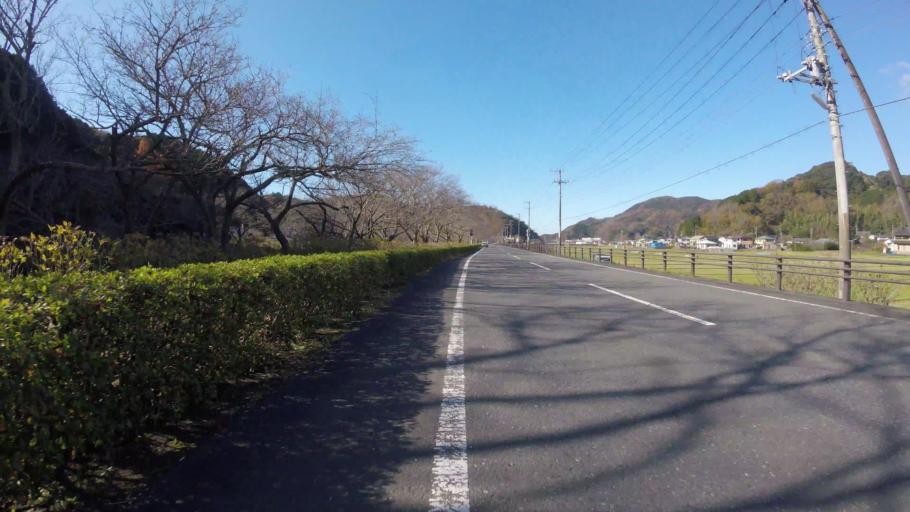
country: JP
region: Shizuoka
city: Shimoda
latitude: 34.7512
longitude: 138.8016
